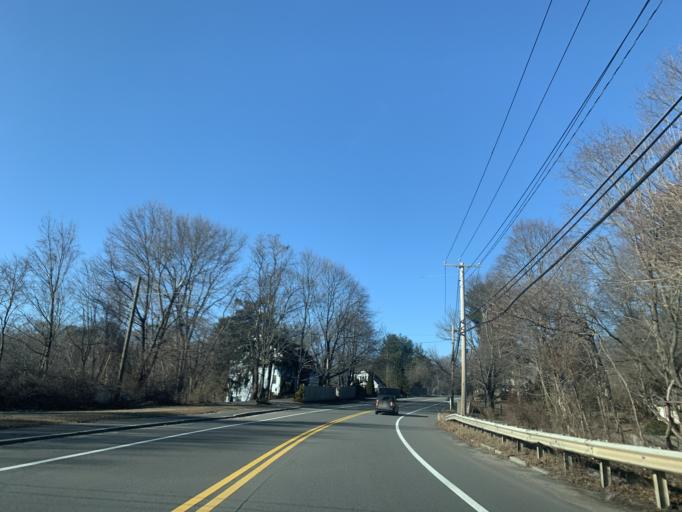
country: US
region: Massachusetts
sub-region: Middlesex County
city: Wayland
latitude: 42.3609
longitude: -71.3466
